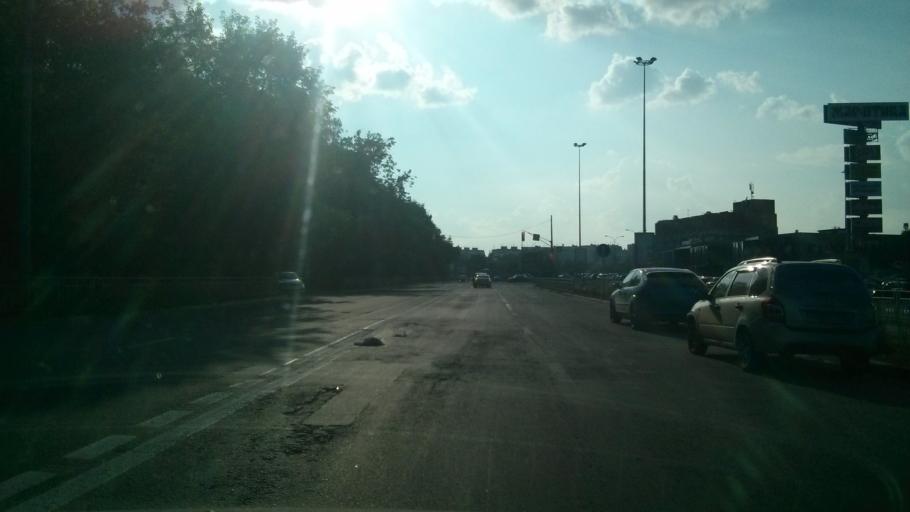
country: RU
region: Nizjnij Novgorod
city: Nizhniy Novgorod
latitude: 56.2949
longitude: 44.0415
